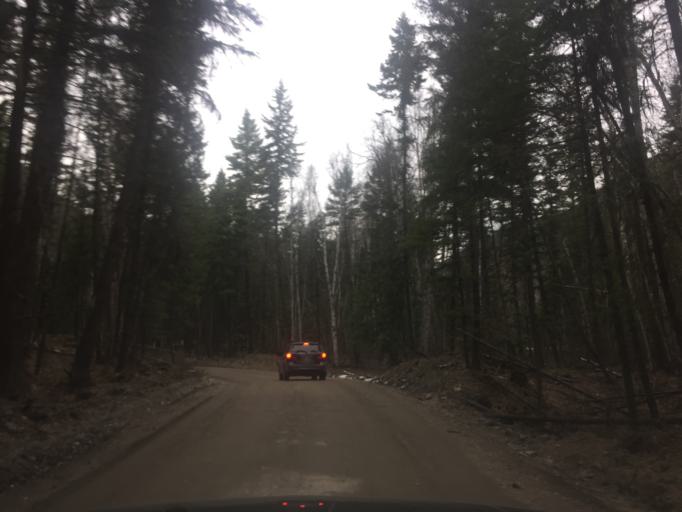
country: CA
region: British Columbia
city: Chase
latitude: 51.3990
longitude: -120.1244
